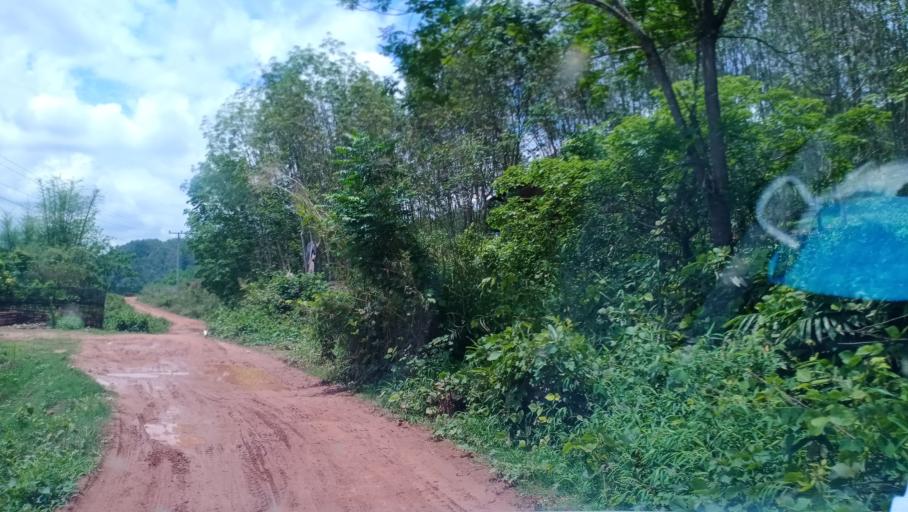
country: CN
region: Yunnan
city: Menglie
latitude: 22.1382
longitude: 101.7825
